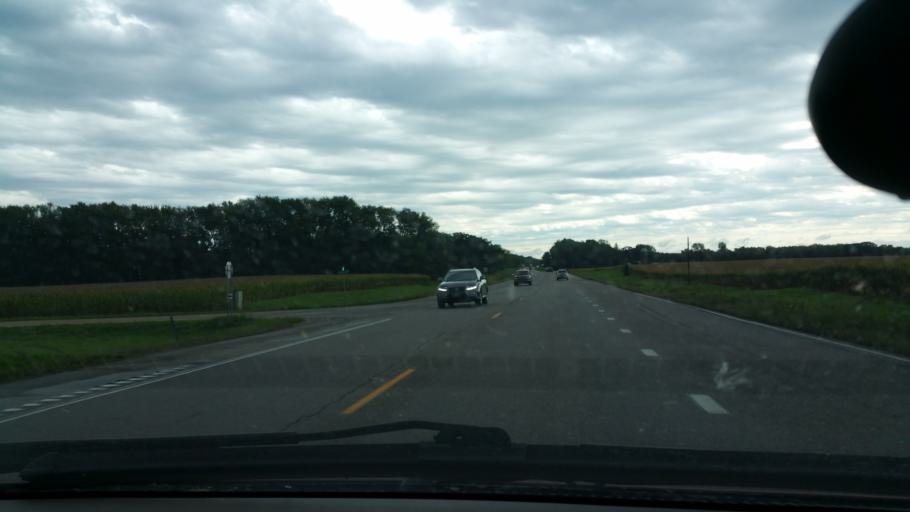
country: US
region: Minnesota
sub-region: Rice County
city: Dundas
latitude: 44.4716
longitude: -93.2422
